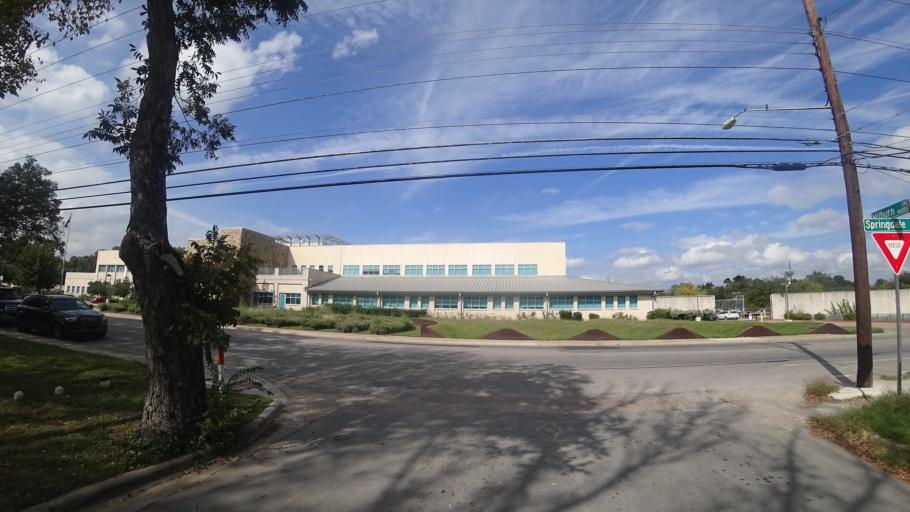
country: US
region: Texas
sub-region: Travis County
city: Austin
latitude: 30.2592
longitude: -97.6995
